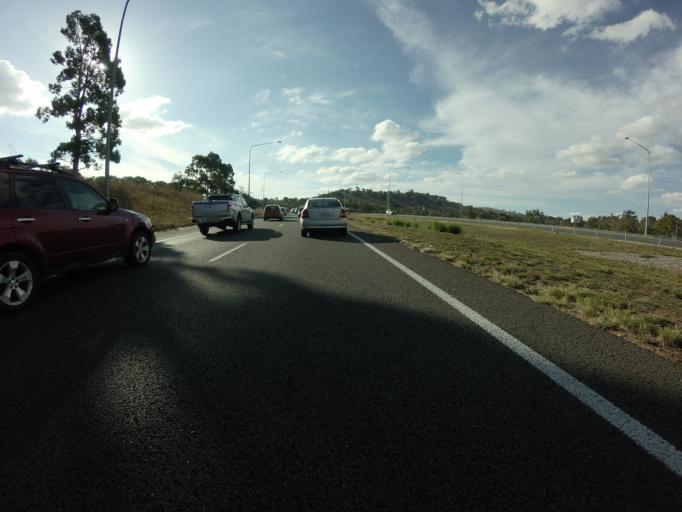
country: AU
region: Australian Capital Territory
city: Kaleen
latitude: -35.2170
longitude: 149.1942
